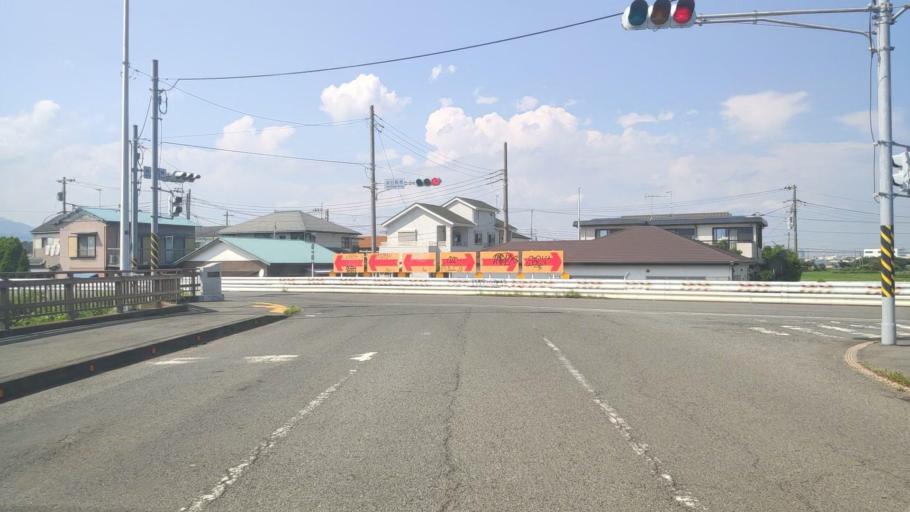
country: JP
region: Kanagawa
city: Isehara
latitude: 35.3669
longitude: 139.3169
